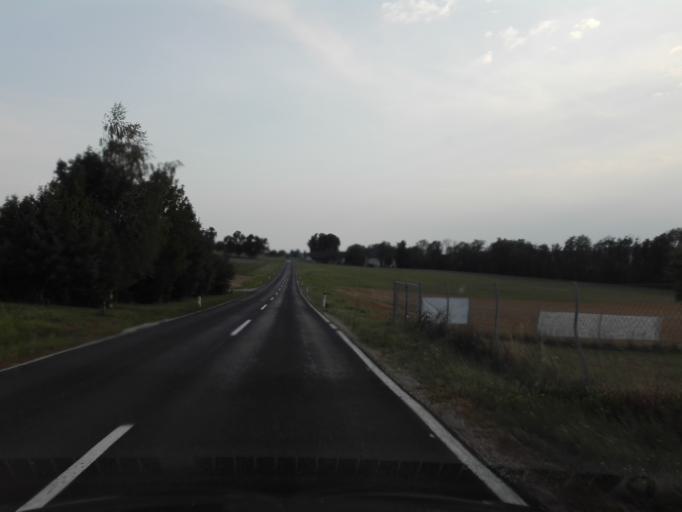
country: AT
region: Upper Austria
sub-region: Politischer Bezirk Grieskirchen
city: Grieskirchen
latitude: 48.2765
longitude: 13.8217
